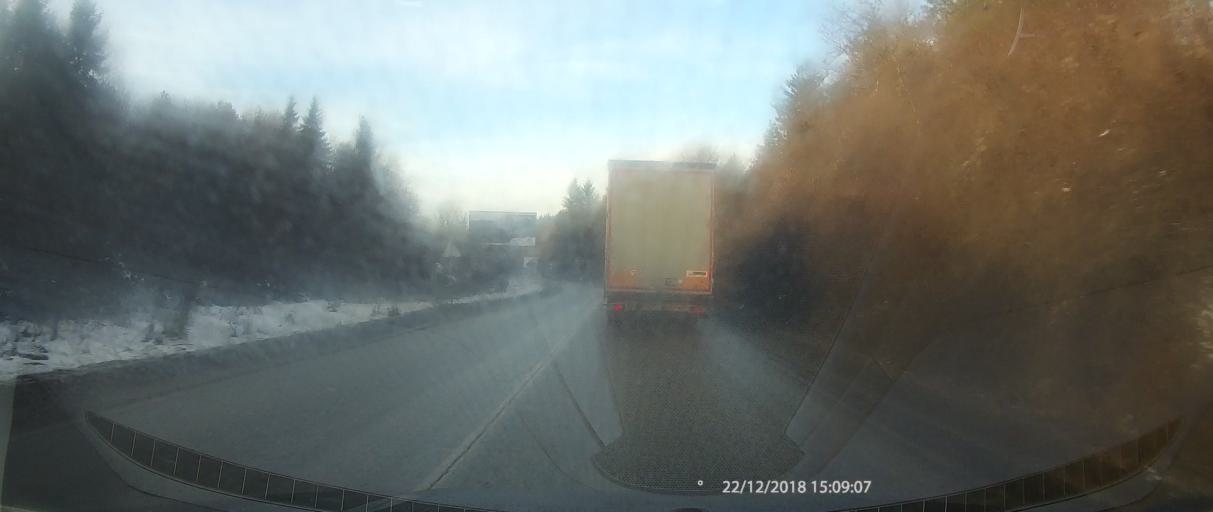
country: BG
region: Ruse
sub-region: Obshtina Borovo
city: Borovo
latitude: 43.4989
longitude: 25.8016
